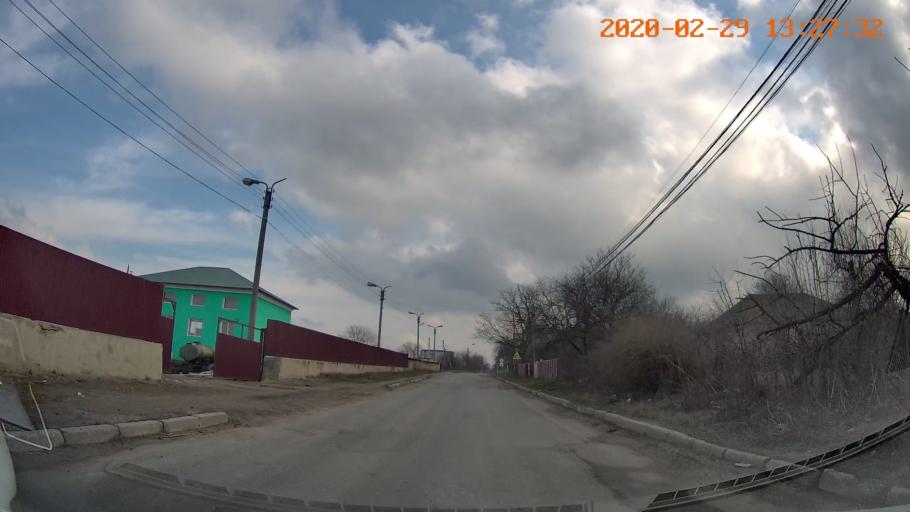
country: MD
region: Telenesti
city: Camenca
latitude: 47.9114
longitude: 28.6425
